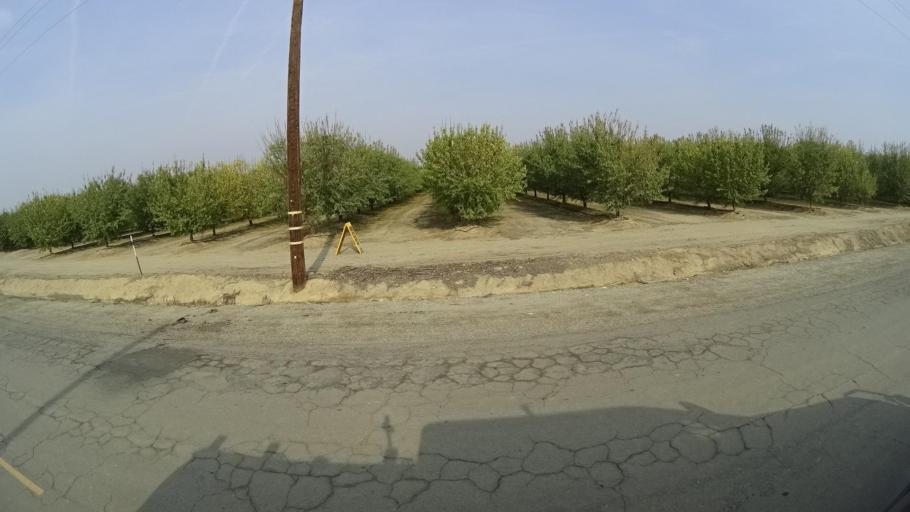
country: US
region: California
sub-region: Kern County
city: Weedpatch
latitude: 35.0763
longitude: -119.0138
